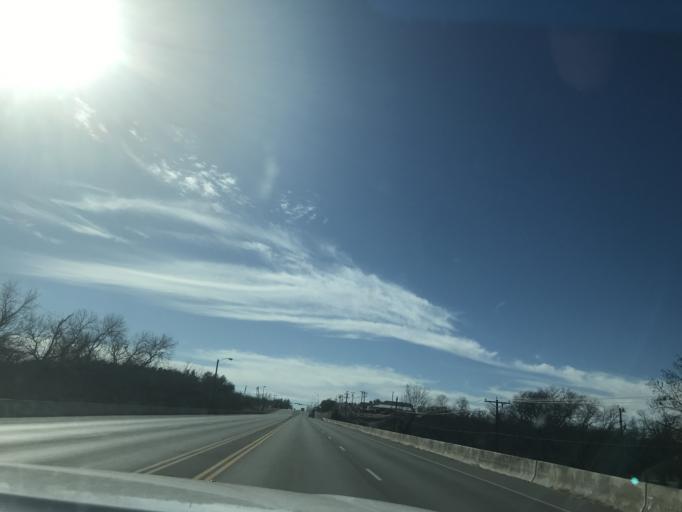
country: US
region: Texas
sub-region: Erath County
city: Stephenville
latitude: 32.2098
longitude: -98.2006
